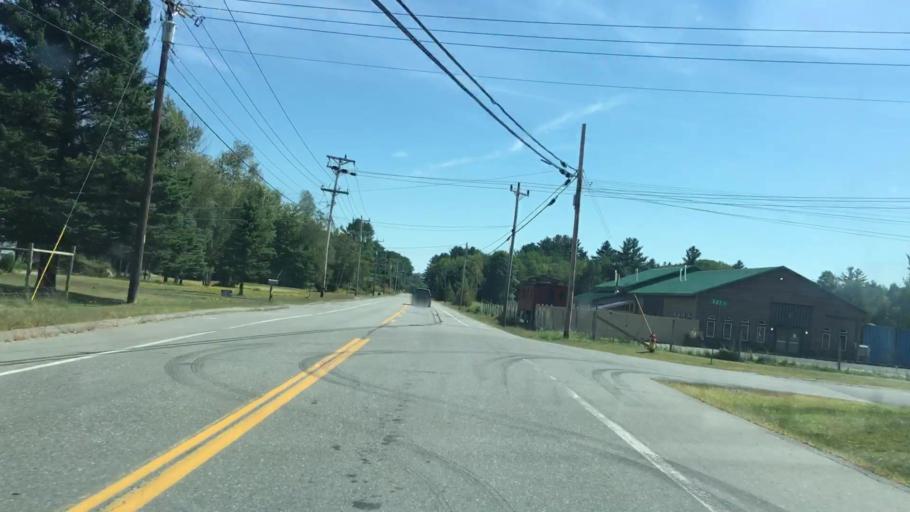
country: US
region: Maine
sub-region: Piscataquis County
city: Milo
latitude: 45.2426
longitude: -68.9728
